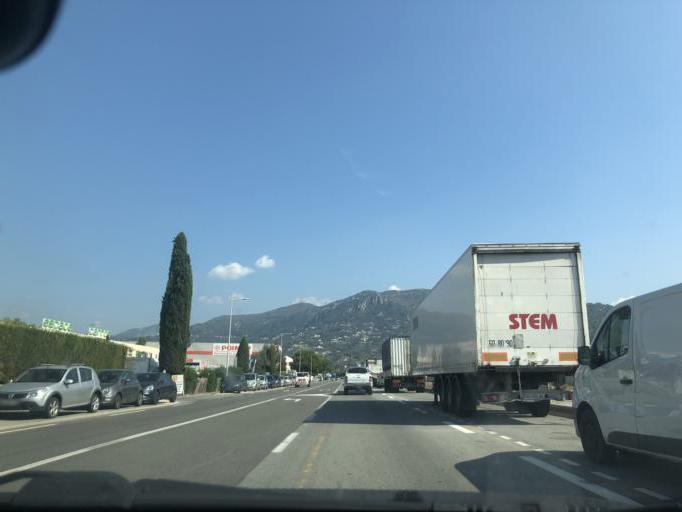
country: FR
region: Provence-Alpes-Cote d'Azur
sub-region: Departement des Alpes-Maritimes
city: Colomars
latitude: 43.7677
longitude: 7.2042
